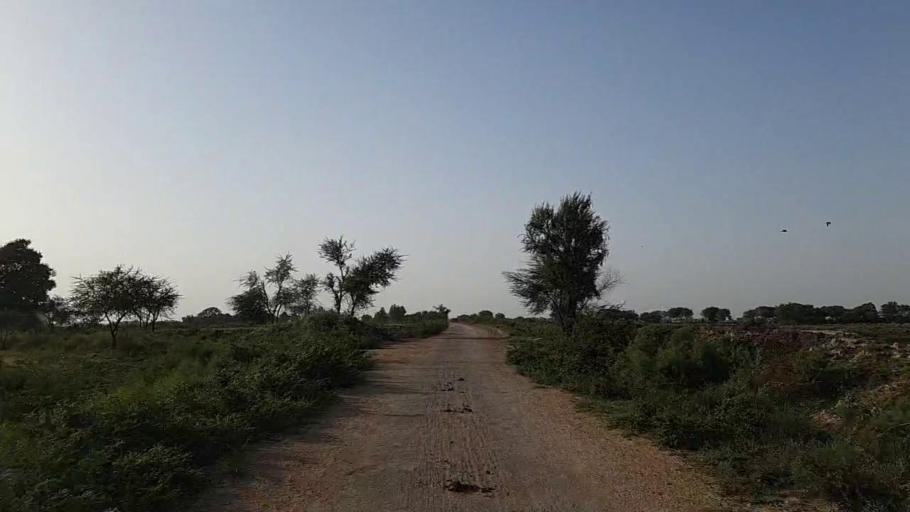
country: PK
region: Sindh
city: Jati
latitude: 24.3254
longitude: 68.1640
